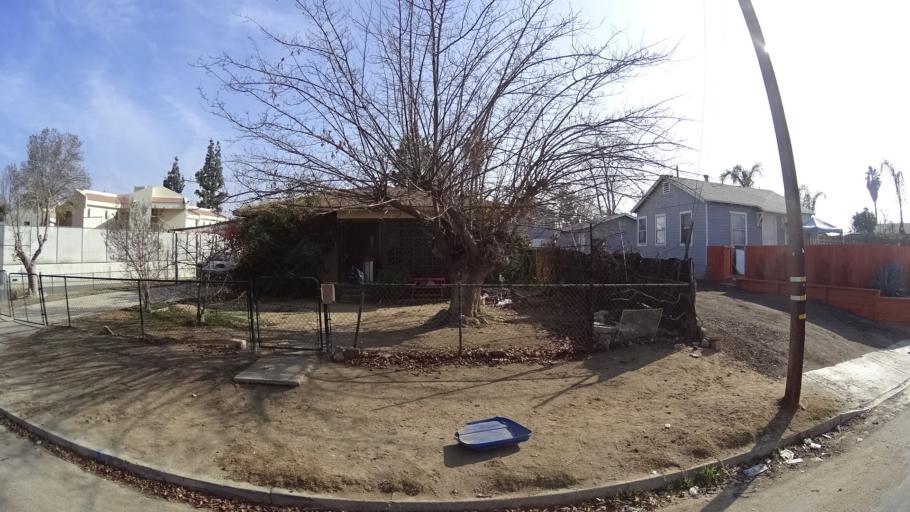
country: US
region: California
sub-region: Kern County
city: Bakersfield
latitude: 35.3857
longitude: -118.9729
